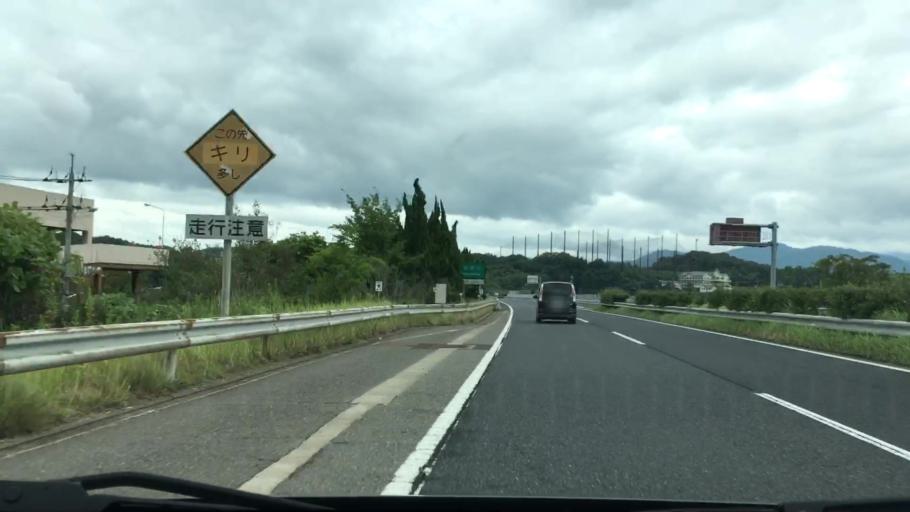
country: JP
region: Okayama
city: Tsuyama
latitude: 35.0658
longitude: 134.0473
